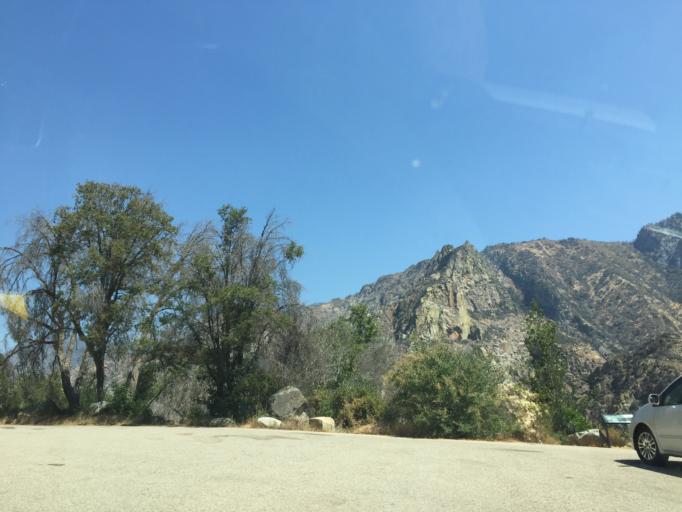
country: US
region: California
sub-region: Tulare County
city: Three Rivers
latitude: 36.8135
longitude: -118.8352
